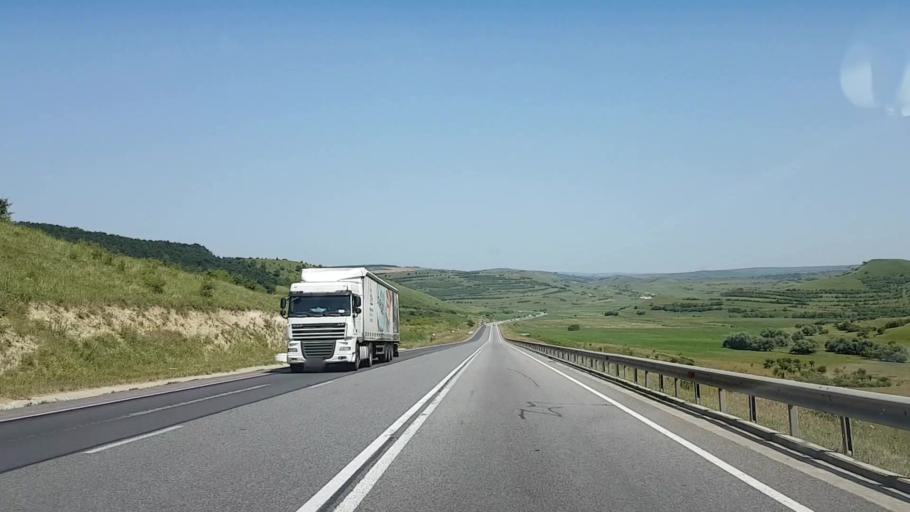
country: RO
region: Cluj
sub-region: Comuna Feleacu
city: Gheorghieni
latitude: 46.7323
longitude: 23.6810
